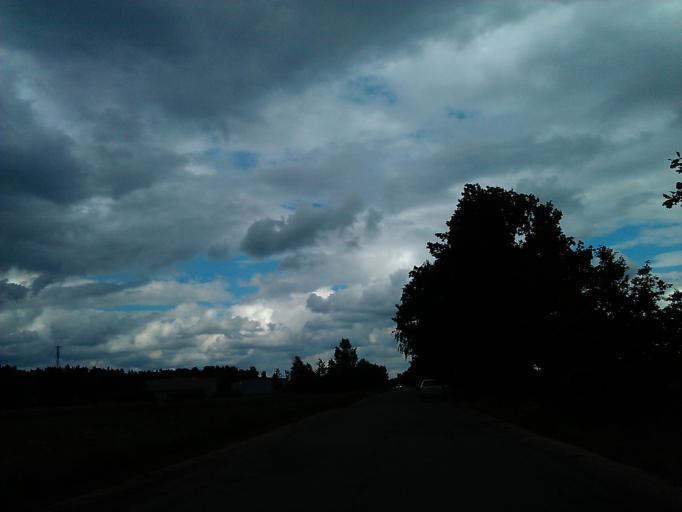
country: LV
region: Adazi
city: Adazi
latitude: 57.0820
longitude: 24.2922
